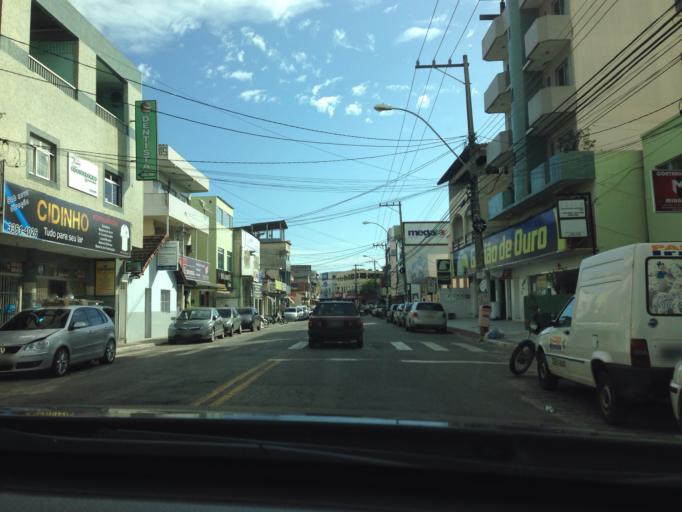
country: BR
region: Espirito Santo
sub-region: Guarapari
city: Guarapari
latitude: -20.6571
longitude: -40.4965
